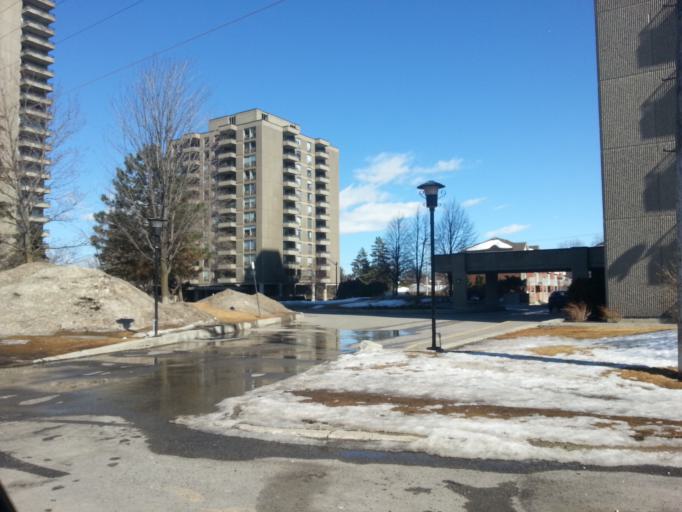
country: CA
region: Ontario
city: Ottawa
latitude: 45.3995
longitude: -75.7518
